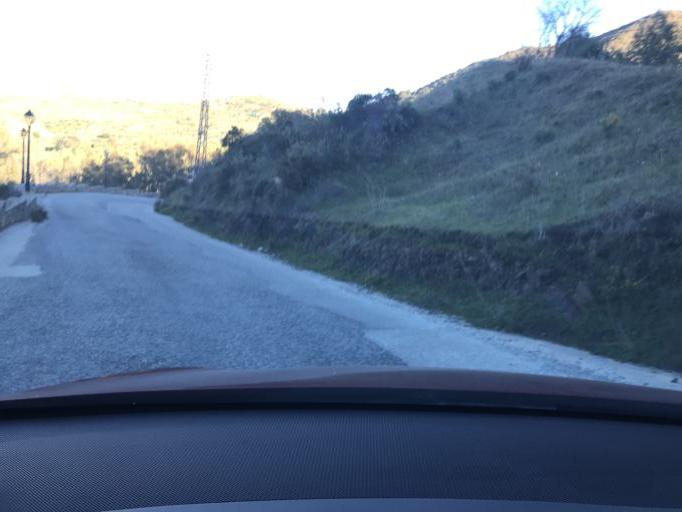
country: ES
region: Andalusia
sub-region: Provincia de Malaga
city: Tolox
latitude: 36.6813
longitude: -4.9102
